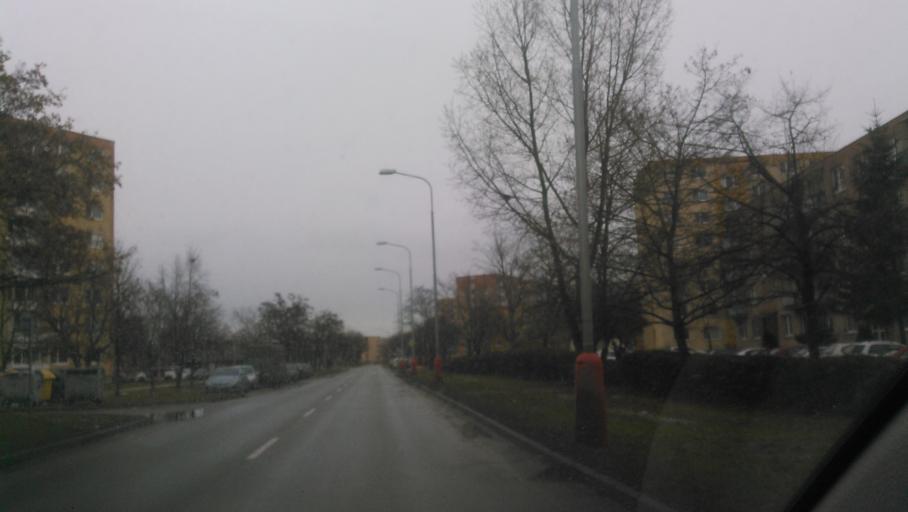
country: SK
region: Nitriansky
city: Sellye
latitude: 48.1476
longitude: 17.8743
